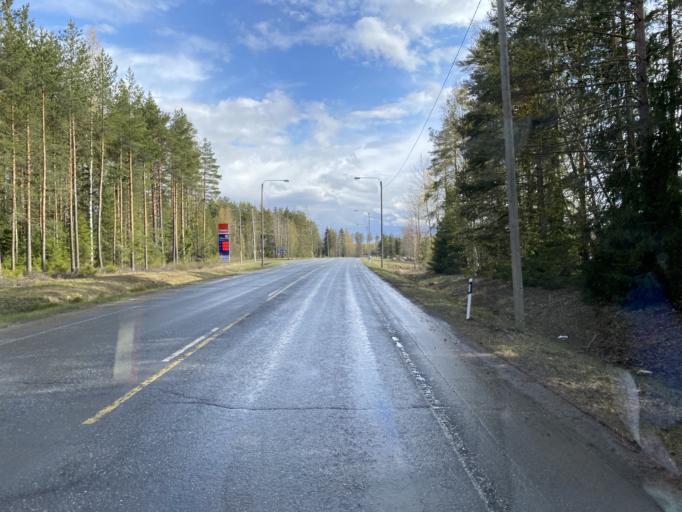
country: FI
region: Pirkanmaa
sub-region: Etelae-Pirkanmaa
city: Viiala
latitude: 61.2044
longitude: 23.7351
